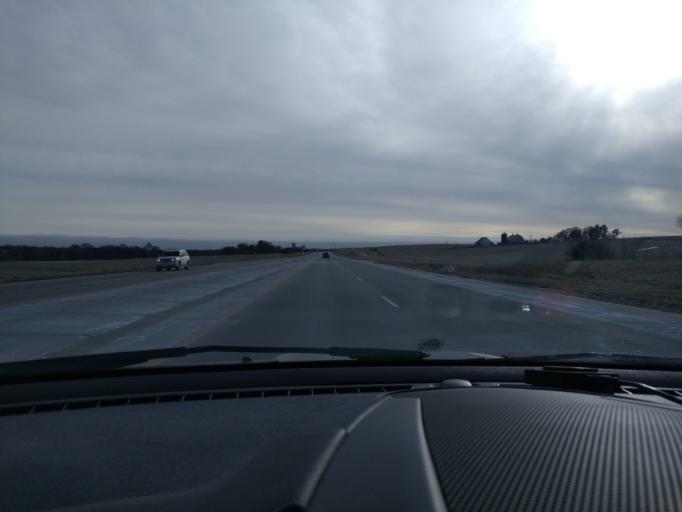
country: US
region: Nebraska
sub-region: Saunders County
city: Wahoo
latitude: 41.2244
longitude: -96.6373
